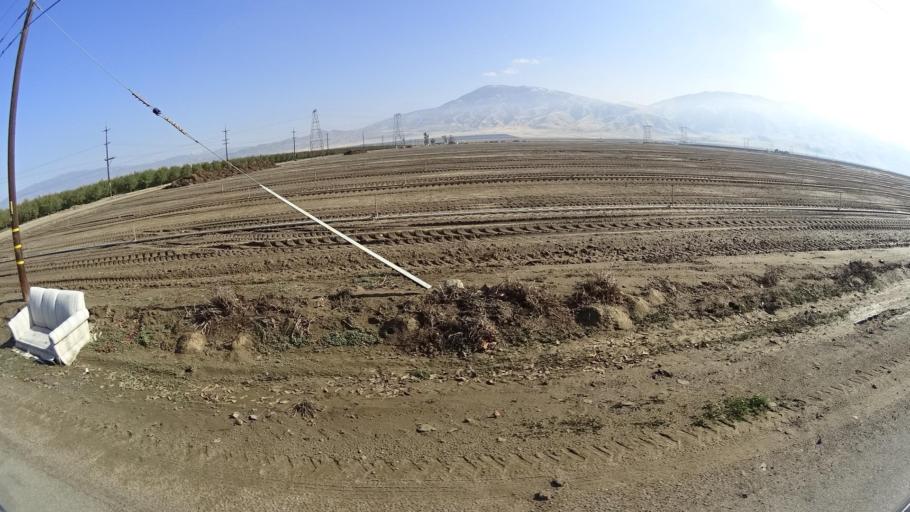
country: US
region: California
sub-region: Kern County
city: Arvin
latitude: 35.2231
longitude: -118.8065
